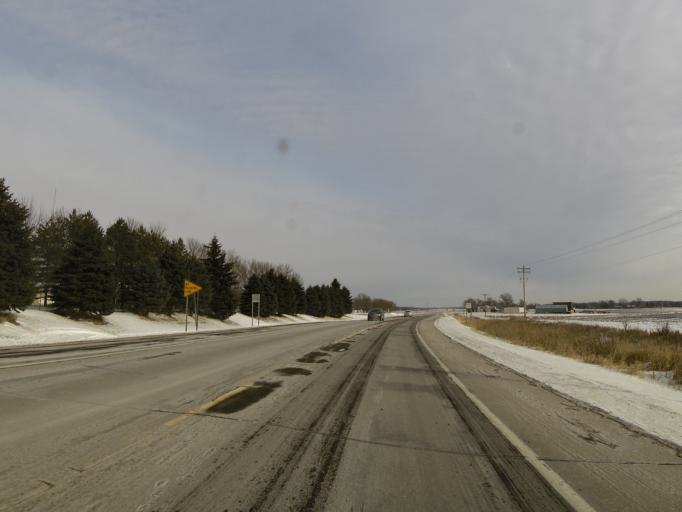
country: US
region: Minnesota
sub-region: Scott County
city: Prior Lake
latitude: 44.6862
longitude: -93.5110
